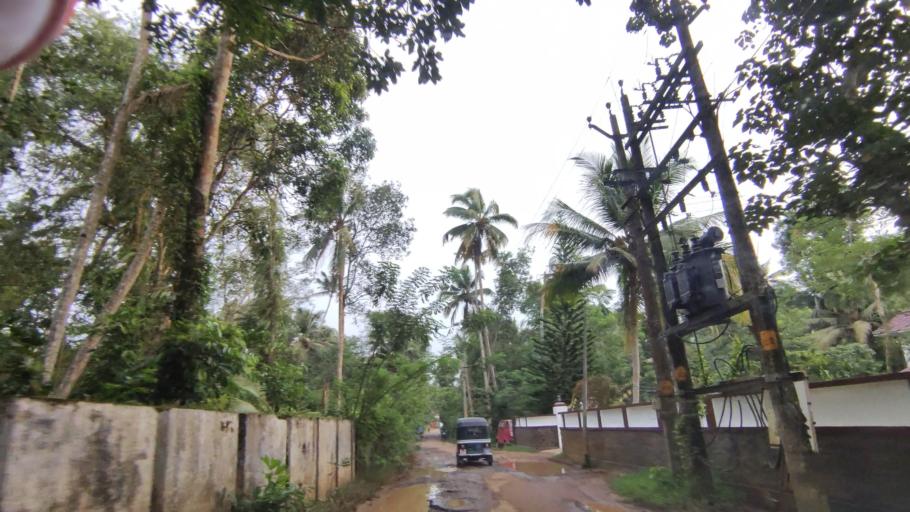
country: IN
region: Kerala
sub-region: Alappuzha
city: Shertallai
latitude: 9.6625
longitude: 76.3642
